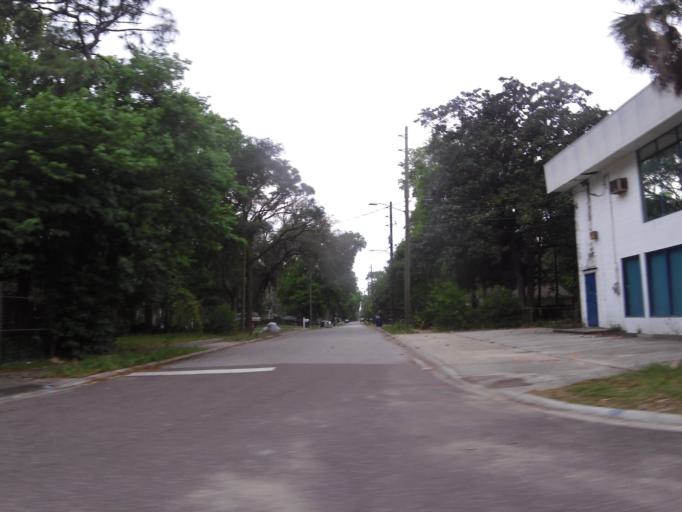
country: US
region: Florida
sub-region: Duval County
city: Jacksonville
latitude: 30.3227
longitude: -81.5607
